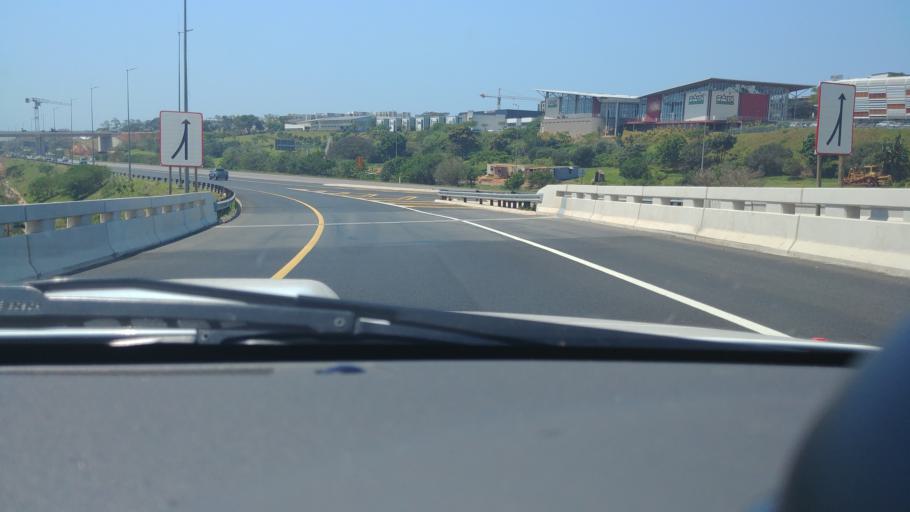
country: ZA
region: KwaZulu-Natal
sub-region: eThekwini Metropolitan Municipality
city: Durban
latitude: -29.7195
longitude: 31.0596
